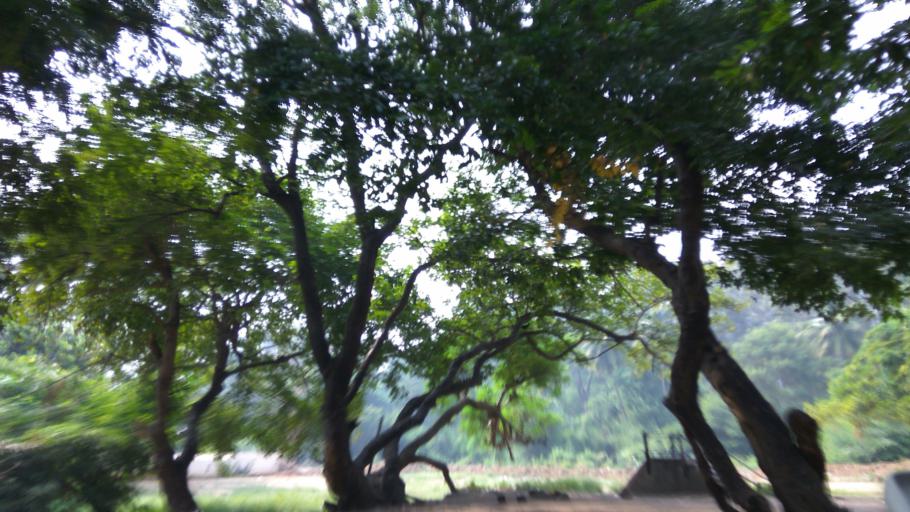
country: IN
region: Tamil Nadu
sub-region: Krishnagiri
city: Krishnagiri
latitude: 12.4730
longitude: 78.1854
